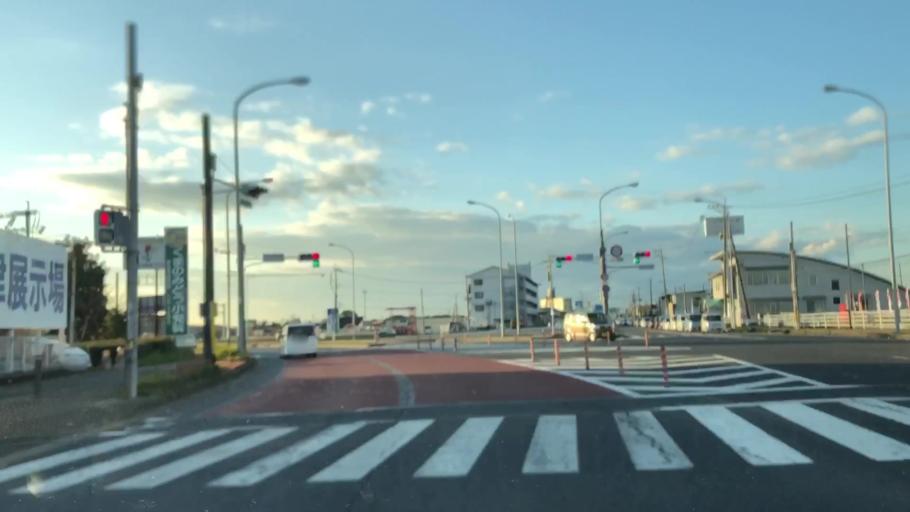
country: JP
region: Fukuoka
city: Nakatsu
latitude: 33.5509
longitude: 131.2742
